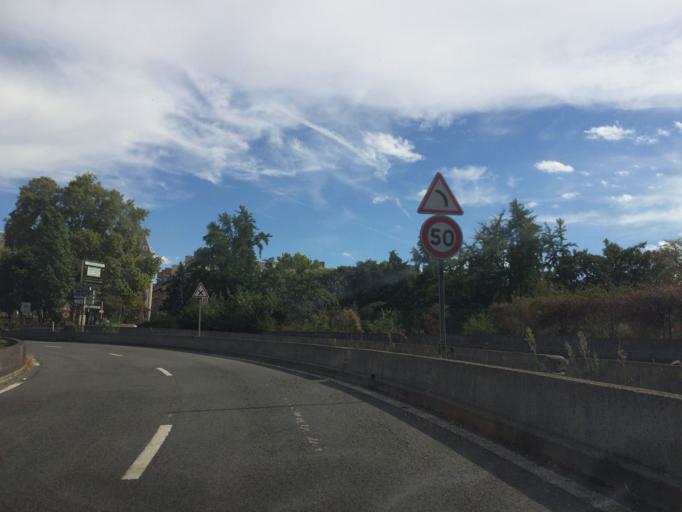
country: FR
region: Ile-de-France
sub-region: Departement des Hauts-de-Seine
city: Neuilly-sur-Seine
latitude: 48.8763
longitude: 2.2777
